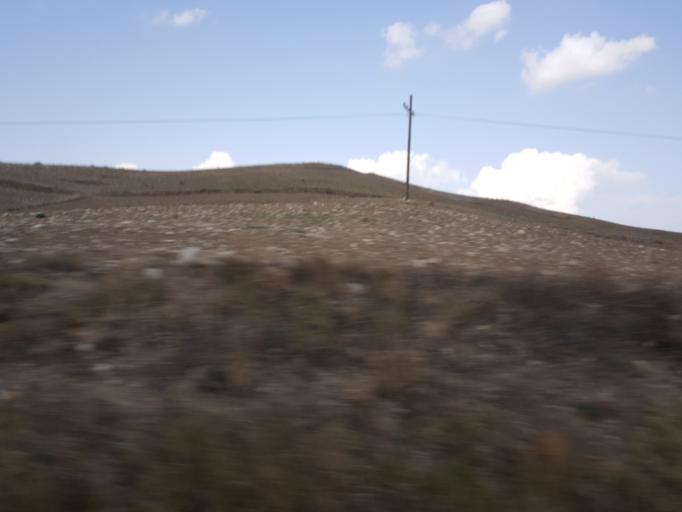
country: TR
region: Corum
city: Bogazkale
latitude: 40.1323
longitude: 34.5498
